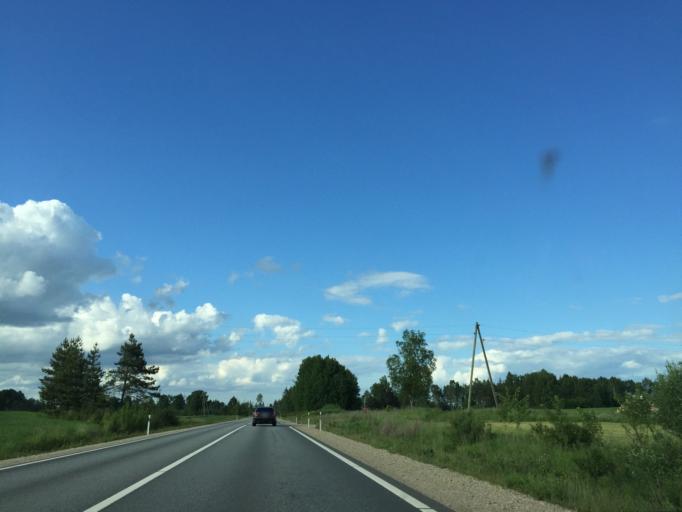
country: LV
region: Dobeles Rajons
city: Dobele
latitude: 56.7127
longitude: 23.1884
